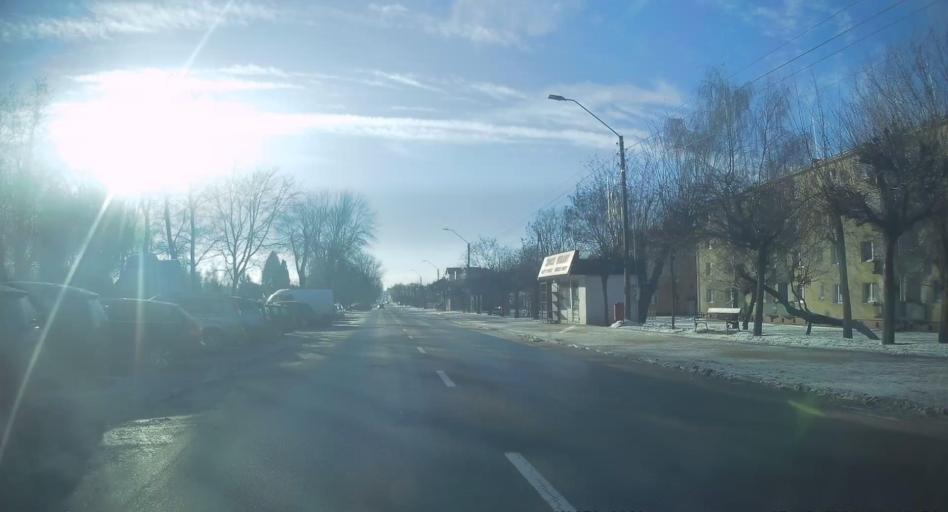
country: PL
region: Lodz Voivodeship
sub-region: Powiat rawski
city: Rawa Mazowiecka
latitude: 51.7587
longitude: 20.2451
